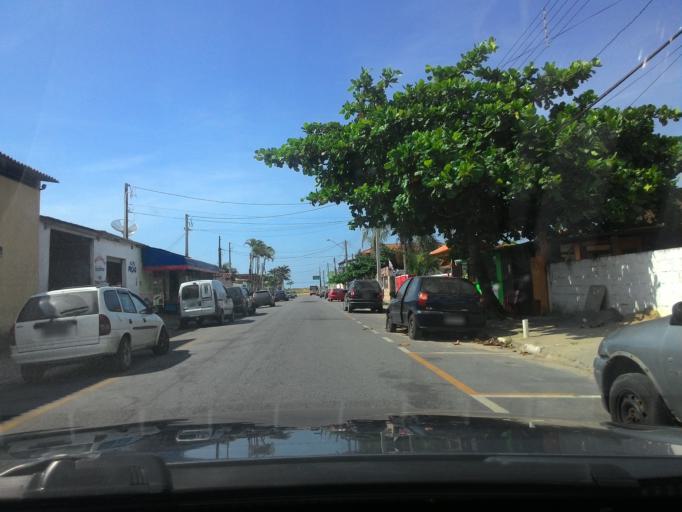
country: BR
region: Sao Paulo
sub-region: Iguape
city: Iguape
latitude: -24.7476
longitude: -47.5531
